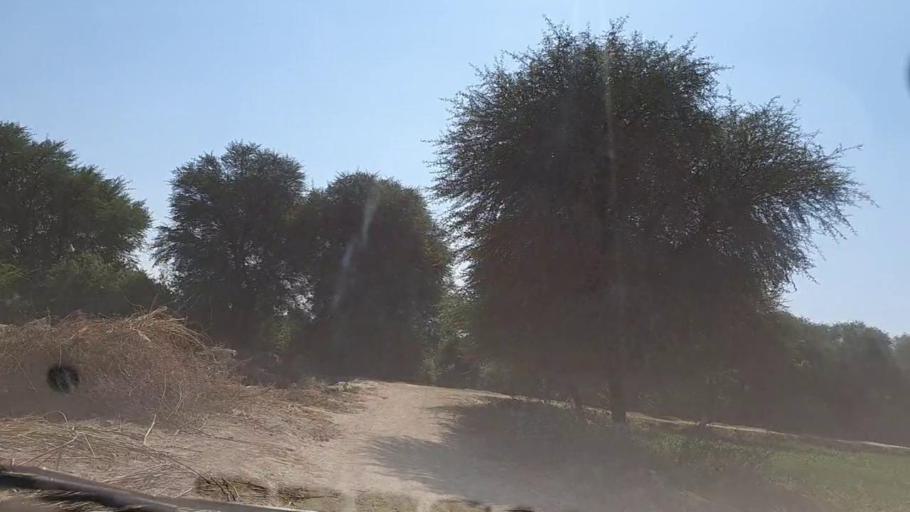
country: PK
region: Sindh
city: Mirpur Khas
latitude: 25.4262
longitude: 69.0559
